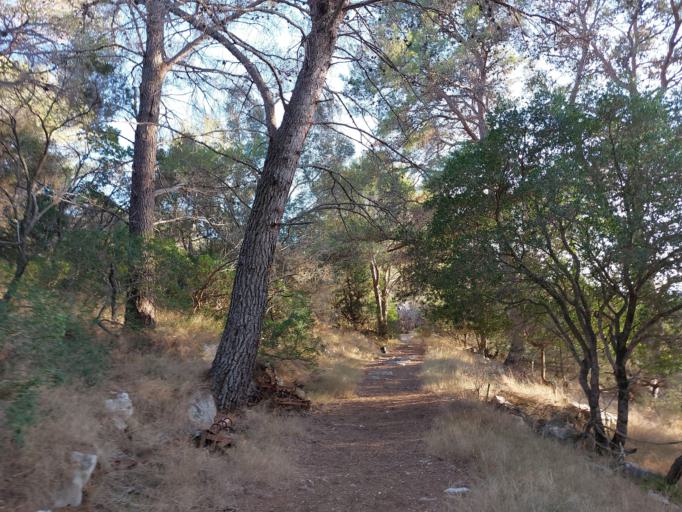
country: HR
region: Dubrovacko-Neretvanska
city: Smokvica
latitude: 42.7726
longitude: 16.7890
